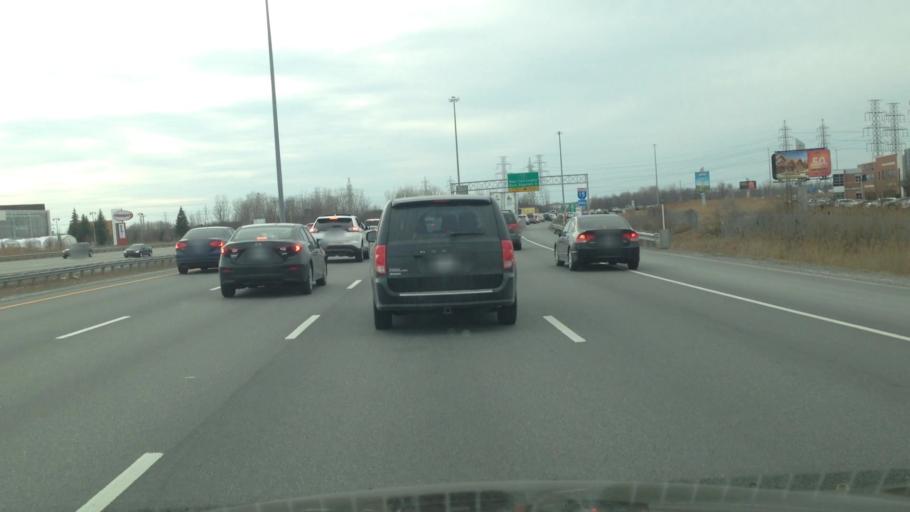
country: CA
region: Quebec
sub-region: Laurentides
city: Rosemere
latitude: 45.5804
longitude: -73.7674
